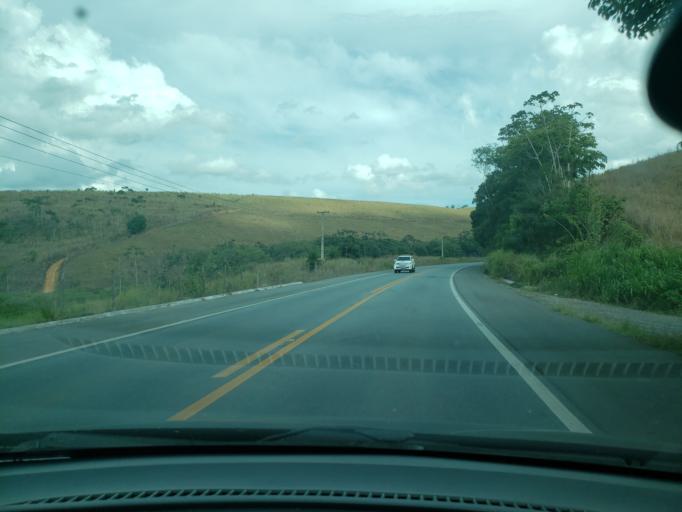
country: BR
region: Alagoas
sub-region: Murici
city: Murici
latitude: -9.2632
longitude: -35.9670
